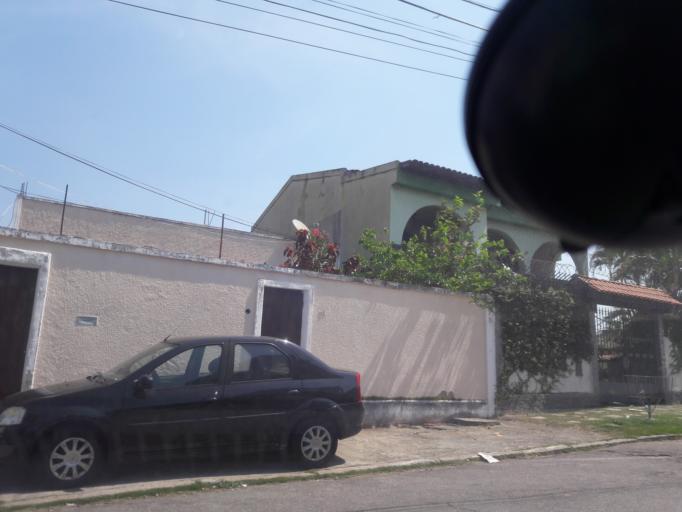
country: BR
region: Rio de Janeiro
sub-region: Sao Joao De Meriti
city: Sao Joao de Meriti
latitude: -22.8786
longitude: -43.3493
